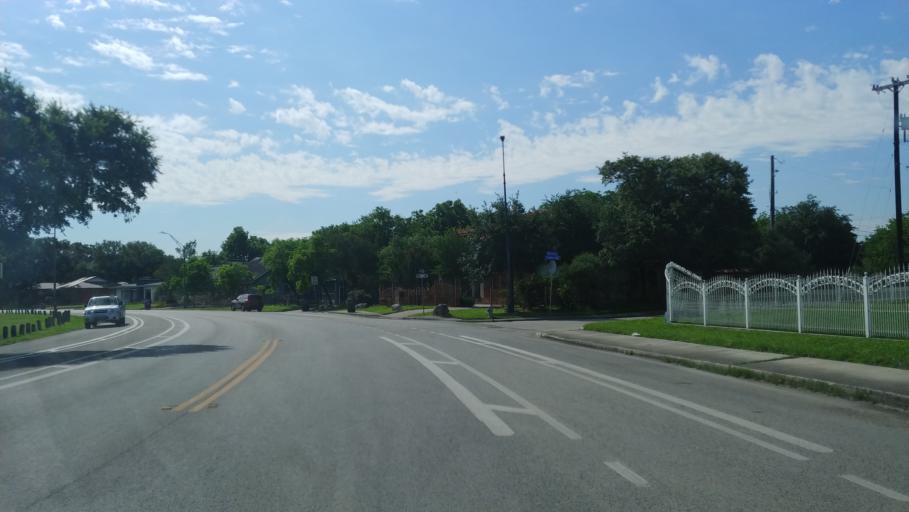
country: US
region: Texas
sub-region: Bexar County
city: Balcones Heights
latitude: 29.4493
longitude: -98.5335
